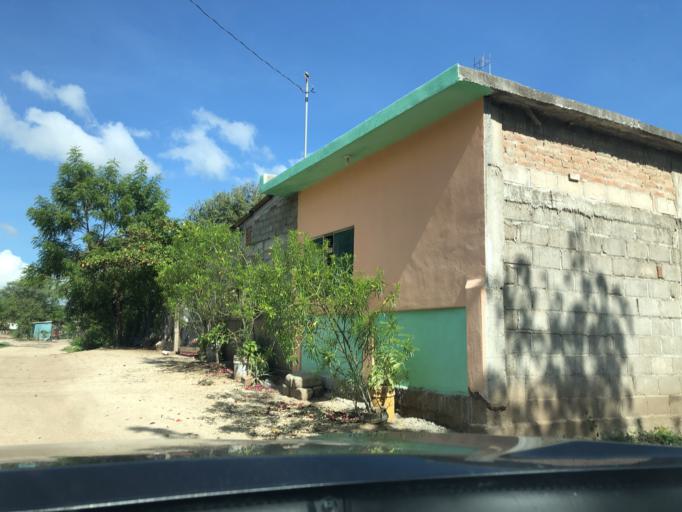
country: MX
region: Oaxaca
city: San Jeronimo Ixtepec
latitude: 16.5525
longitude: -95.1057
